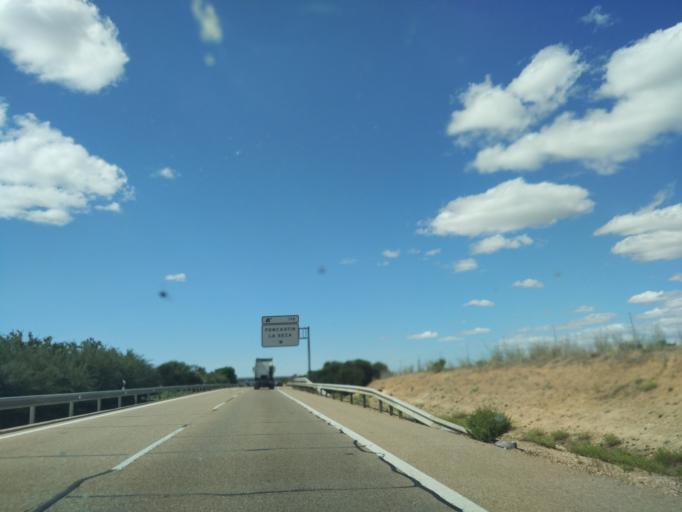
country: ES
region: Castille and Leon
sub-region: Provincia de Valladolid
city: Rueda
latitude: 41.4395
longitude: -4.9748
